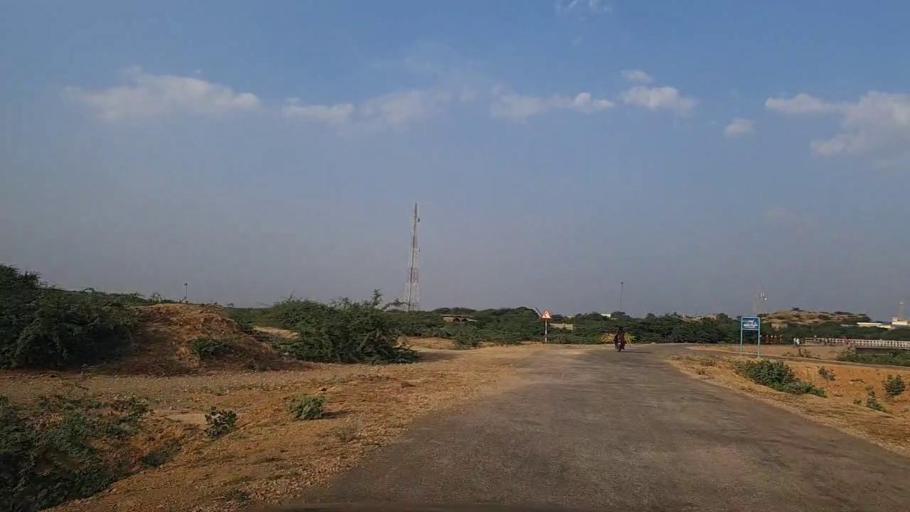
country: PK
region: Sindh
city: Thatta
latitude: 24.8498
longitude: 67.7688
